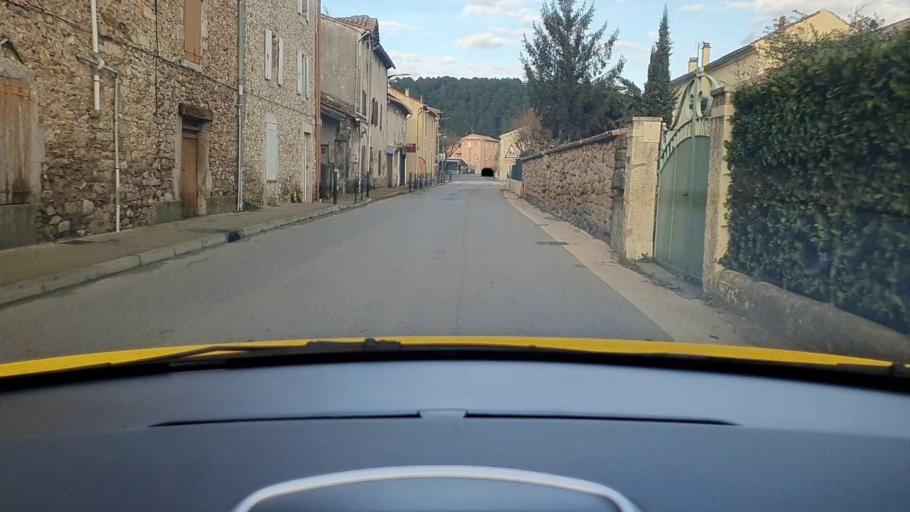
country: FR
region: Languedoc-Roussillon
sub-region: Departement du Gard
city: Laval-Pradel
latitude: 44.2309
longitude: 4.0590
